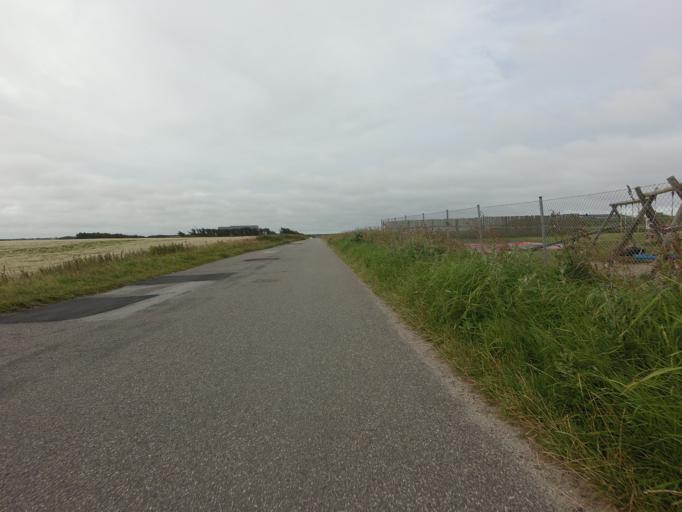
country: DK
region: North Denmark
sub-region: Jammerbugt Kommune
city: Pandrup
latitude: 57.3846
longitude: 9.7250
